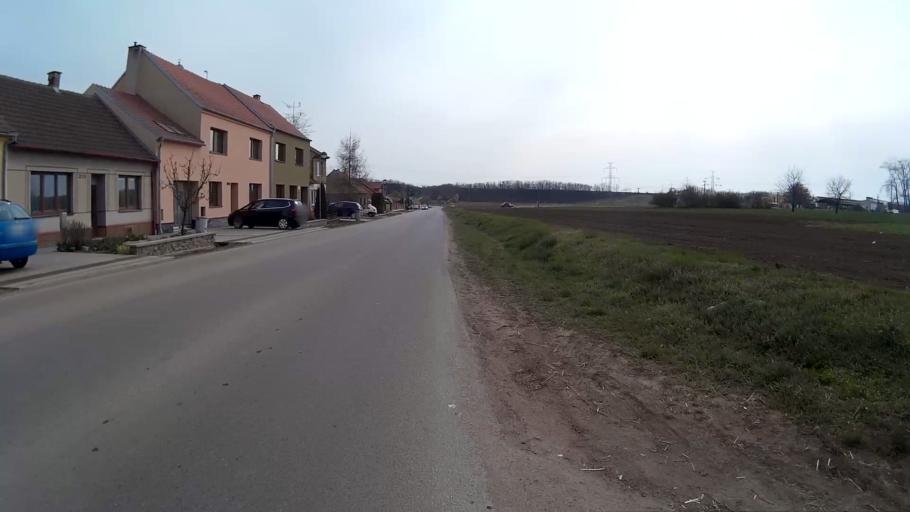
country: CZ
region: South Moravian
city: Orechov
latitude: 49.0643
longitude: 16.5211
